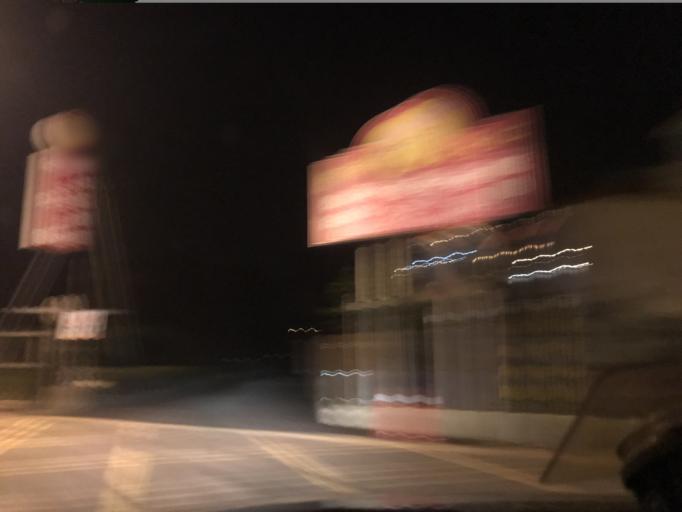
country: TW
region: Taiwan
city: Daxi
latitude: 24.8511
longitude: 121.2157
